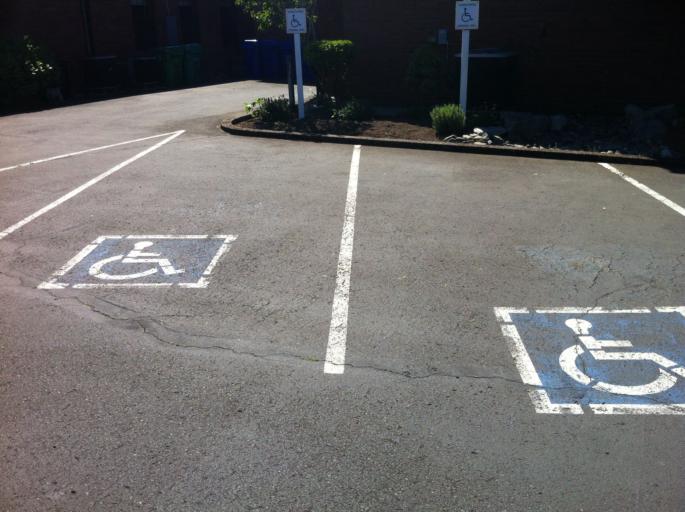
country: US
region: Oregon
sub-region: Multnomah County
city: Lents
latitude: 45.5031
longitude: -122.5936
